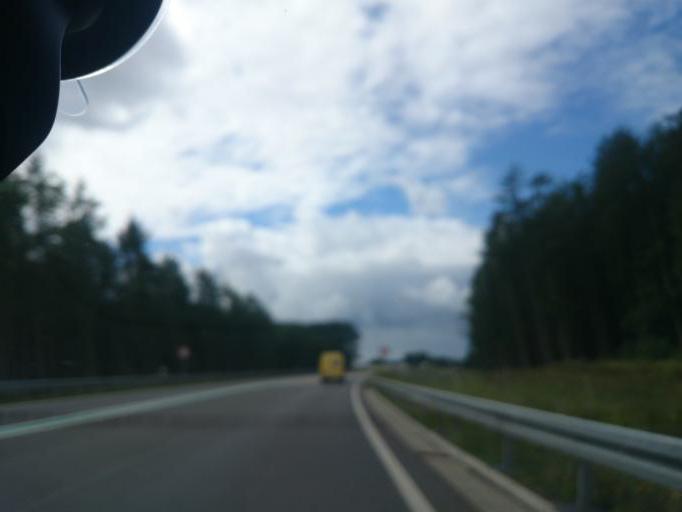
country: DE
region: Mecklenburg-Vorpommern
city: Samtens
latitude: 54.3582
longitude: 13.3099
